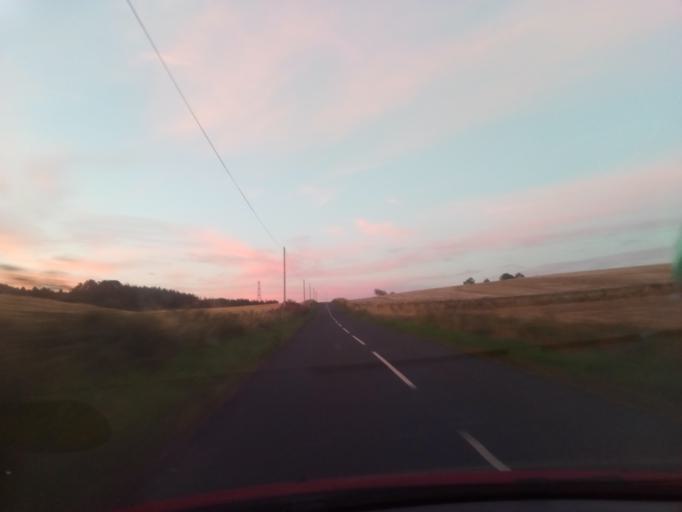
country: GB
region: England
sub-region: Northumberland
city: Wall
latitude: 55.0092
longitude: -2.1739
